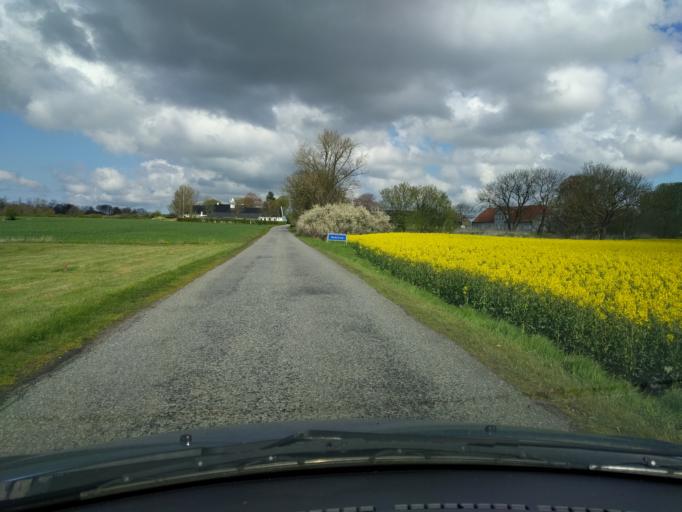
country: DK
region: South Denmark
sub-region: Kerteminde Kommune
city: Munkebo
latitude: 55.4082
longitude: 10.5416
